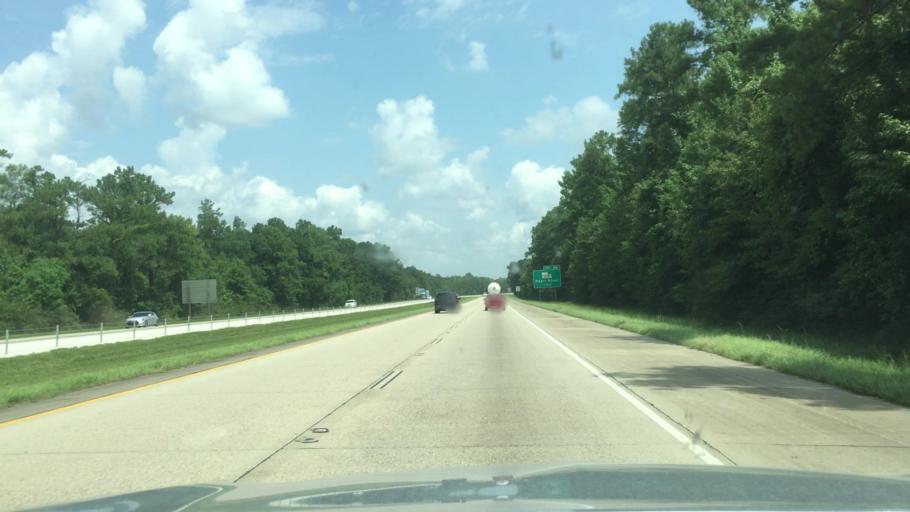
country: US
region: Louisiana
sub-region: Saint Tammany Parish
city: Pearl River
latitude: 30.3598
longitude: -89.7417
